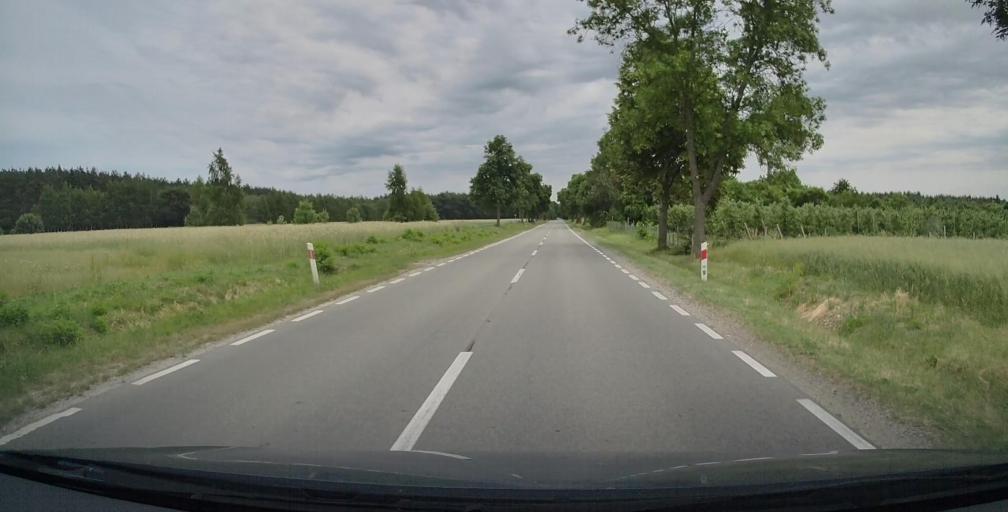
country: PL
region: Masovian Voivodeship
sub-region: Powiat losicki
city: Sarnaki
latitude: 52.3105
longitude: 22.9141
